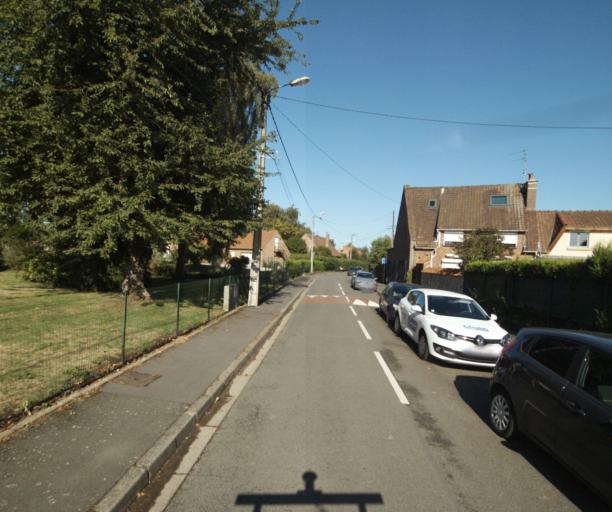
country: FR
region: Nord-Pas-de-Calais
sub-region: Departement du Nord
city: Toufflers
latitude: 50.6490
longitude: 3.2308
